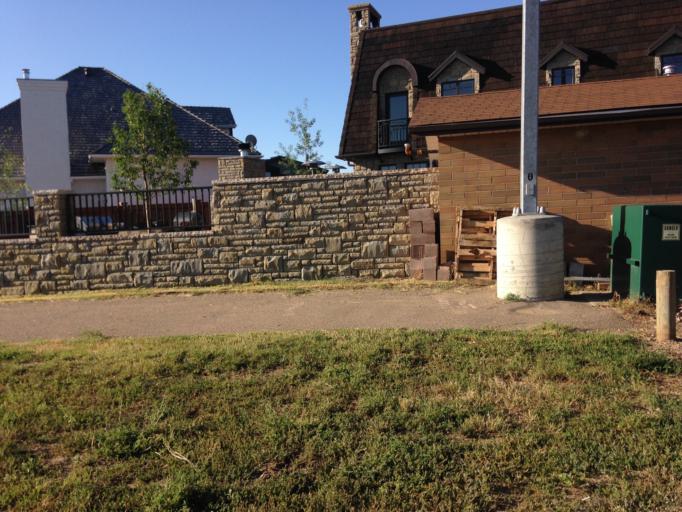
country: CA
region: Alberta
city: Medicine Hat
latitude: 50.0014
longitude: -110.6235
